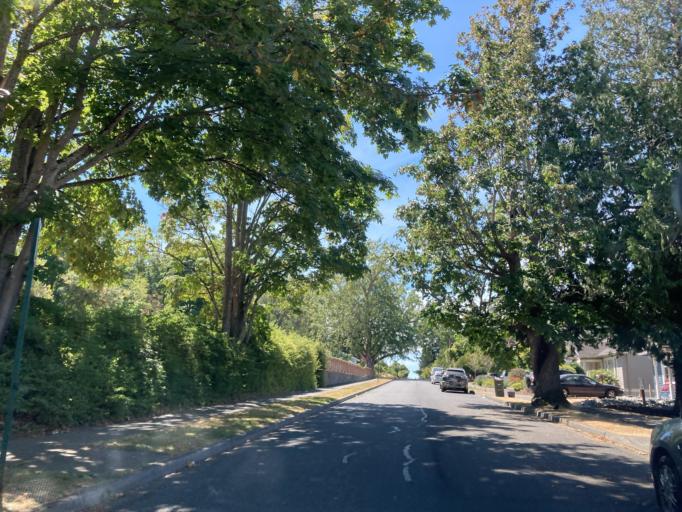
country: US
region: Washington
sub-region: Whatcom County
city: Bellingham
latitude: 48.7405
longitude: -122.4867
